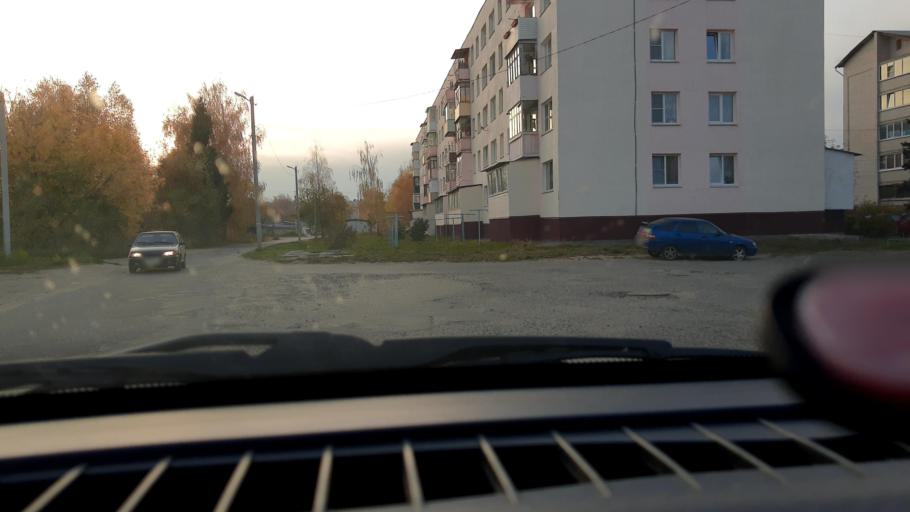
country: RU
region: Nizjnij Novgorod
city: Gorodets
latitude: 56.6371
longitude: 43.4863
